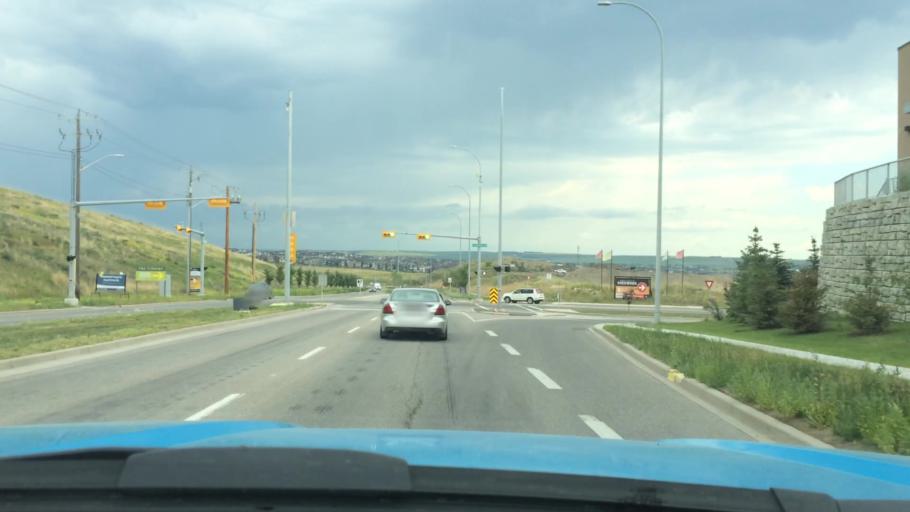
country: CA
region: Alberta
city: Calgary
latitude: 51.1620
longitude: -114.1627
